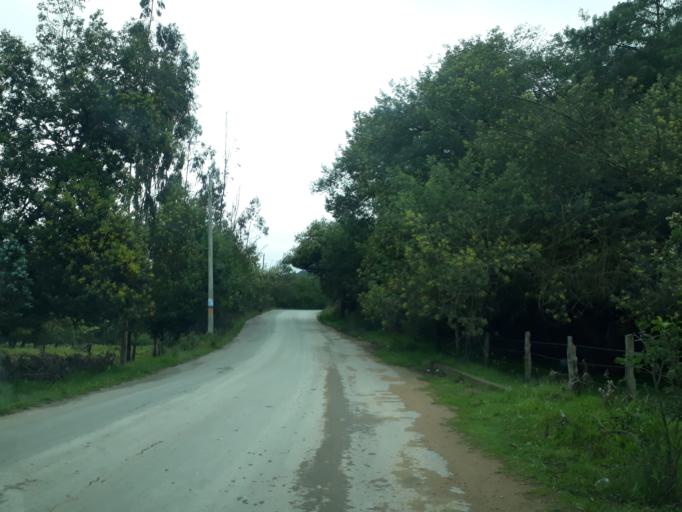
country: CO
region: Cundinamarca
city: Cucunuba
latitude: 5.1925
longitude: -73.7876
